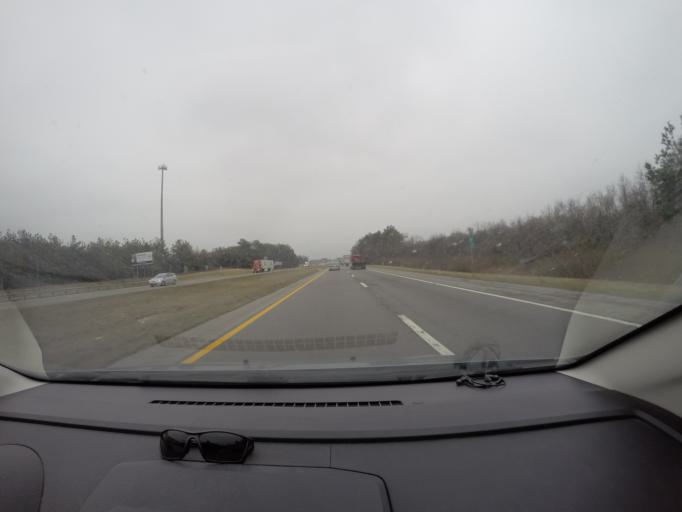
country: US
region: Tennessee
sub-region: Rutherford County
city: Murfreesboro
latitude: 35.7928
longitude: -86.3773
